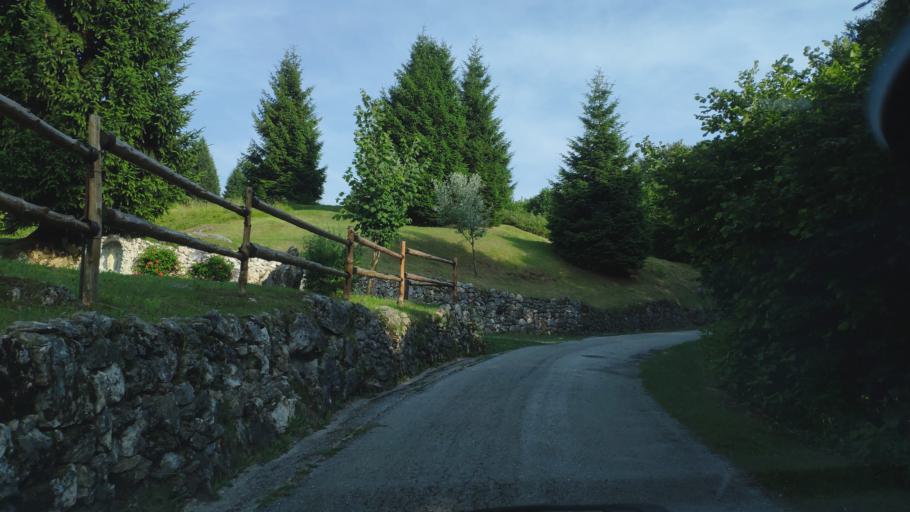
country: IT
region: Veneto
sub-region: Provincia di Vicenza
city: Cogollo del Cengio
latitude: 45.8083
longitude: 11.4336
